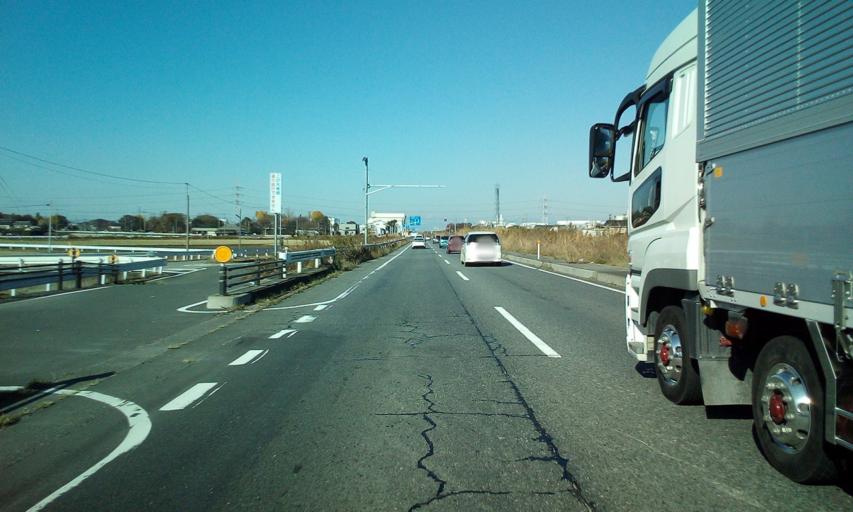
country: JP
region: Ibaraki
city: Sakai
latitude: 36.0732
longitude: 139.7733
